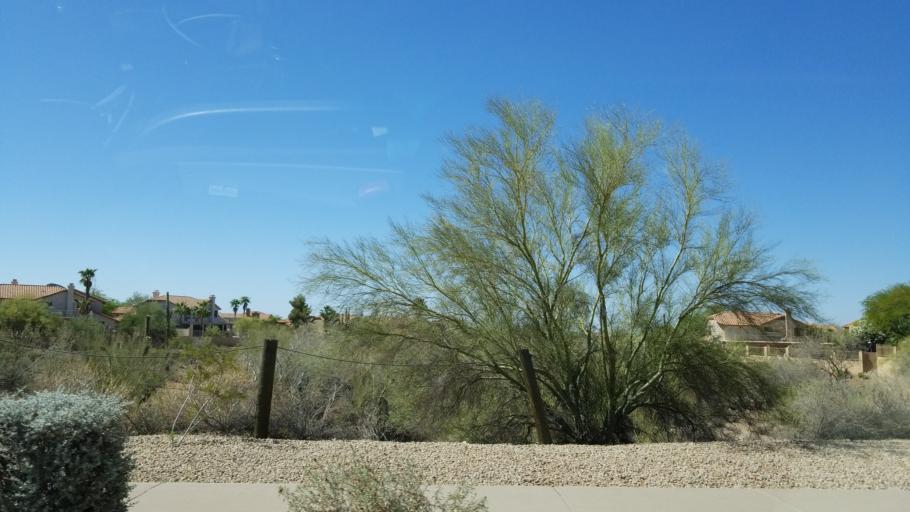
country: US
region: Arizona
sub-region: Maricopa County
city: Fountain Hills
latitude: 33.5896
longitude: -111.8028
